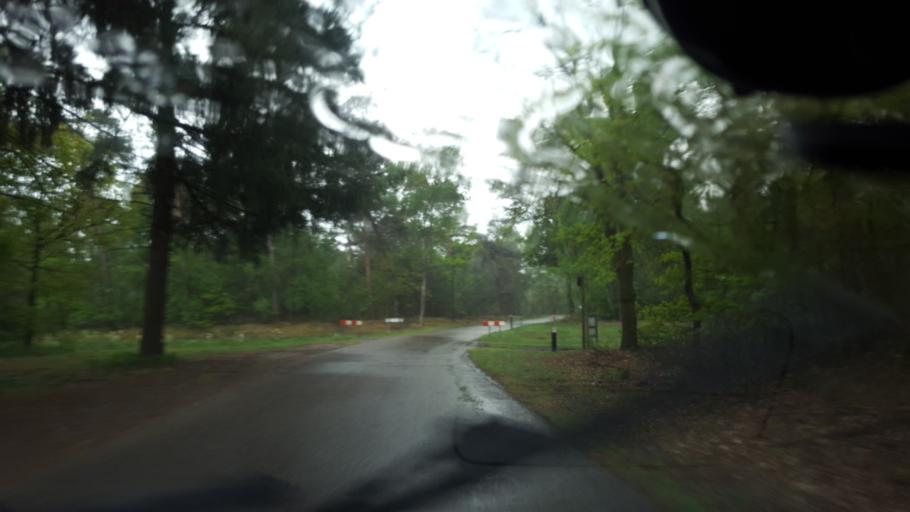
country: NL
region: North Brabant
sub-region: Gemeente Someren
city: Someren
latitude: 51.3968
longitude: 5.6711
